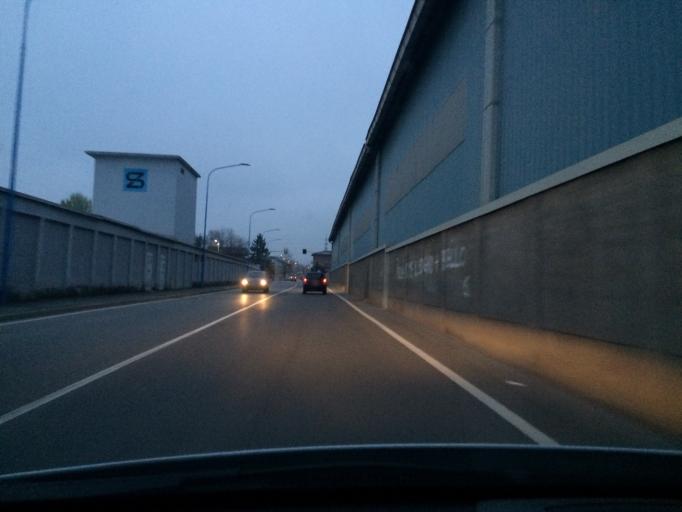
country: IT
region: Lombardy
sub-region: Provincia di Brescia
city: Folzano
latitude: 45.4944
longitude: 10.2109
